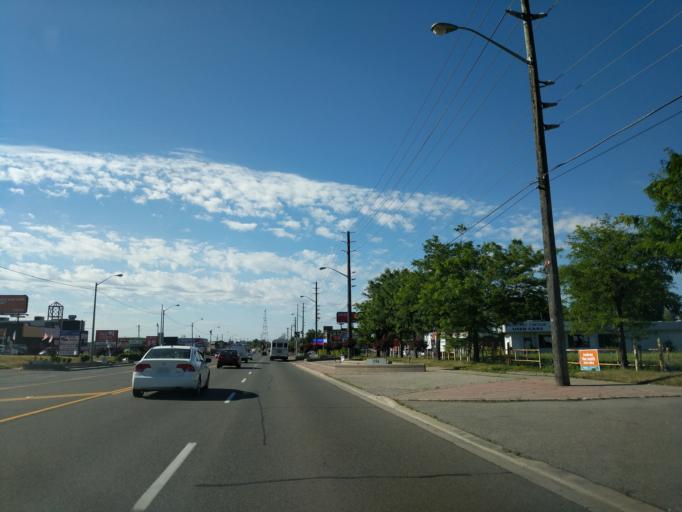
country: CA
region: Ontario
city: Scarborough
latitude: 43.7589
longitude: -79.2785
